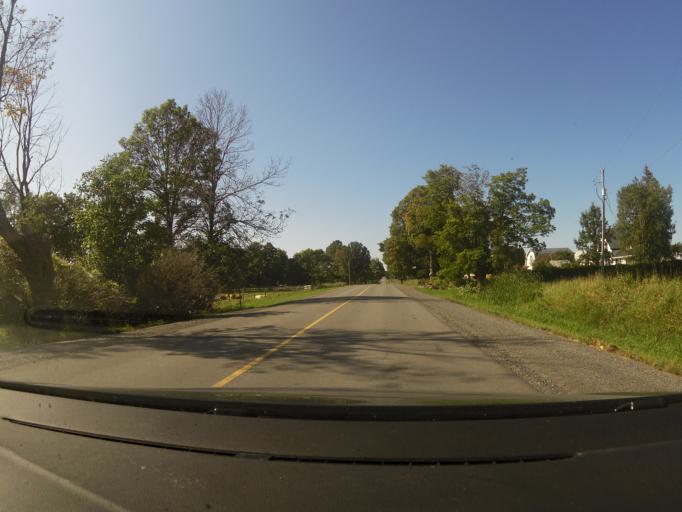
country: CA
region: Ontario
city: Arnprior
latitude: 45.3881
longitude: -76.1369
